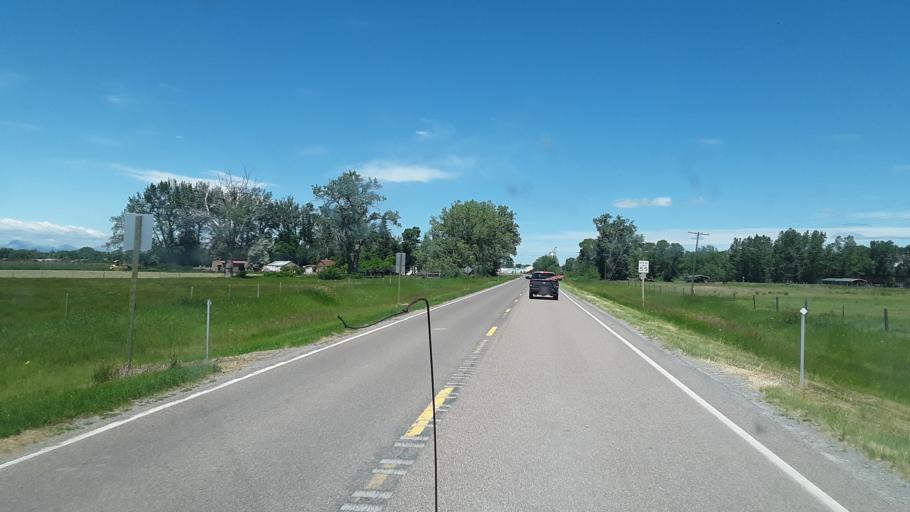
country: US
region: Montana
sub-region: Teton County
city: Choteau
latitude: 47.7996
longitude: -112.1718
